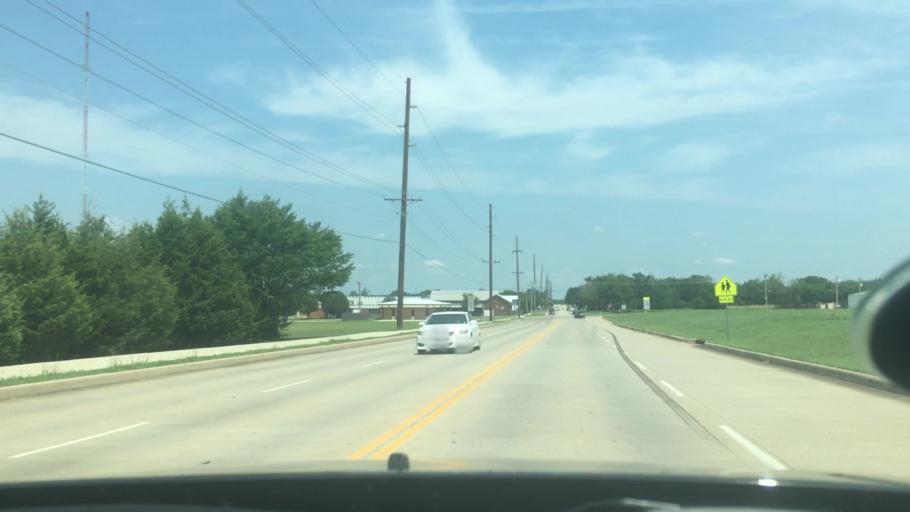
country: US
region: Oklahoma
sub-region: Pottawatomie County
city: Shawnee
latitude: 35.3594
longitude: -96.8943
